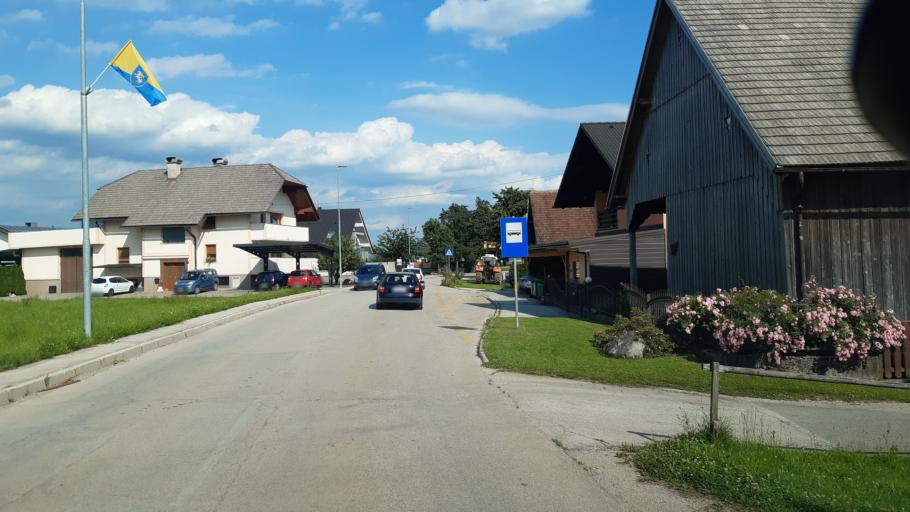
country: SI
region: Sencur
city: Hrastje
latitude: 46.2144
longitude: 14.3912
